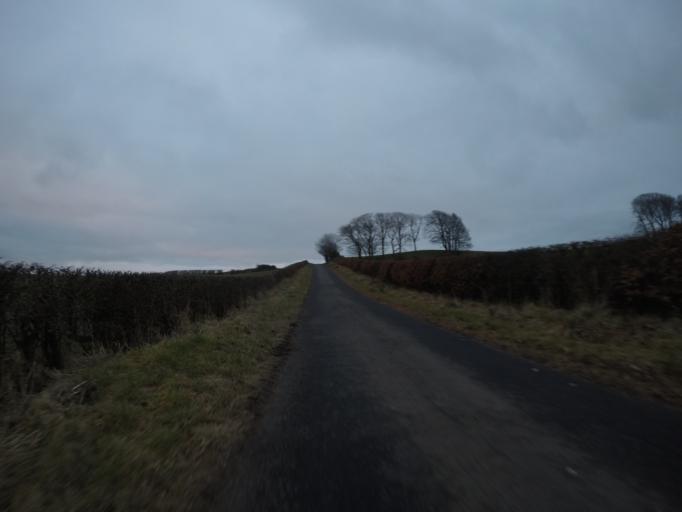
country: GB
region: Scotland
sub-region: North Ayrshire
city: Dalry
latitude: 55.6857
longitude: -4.7342
